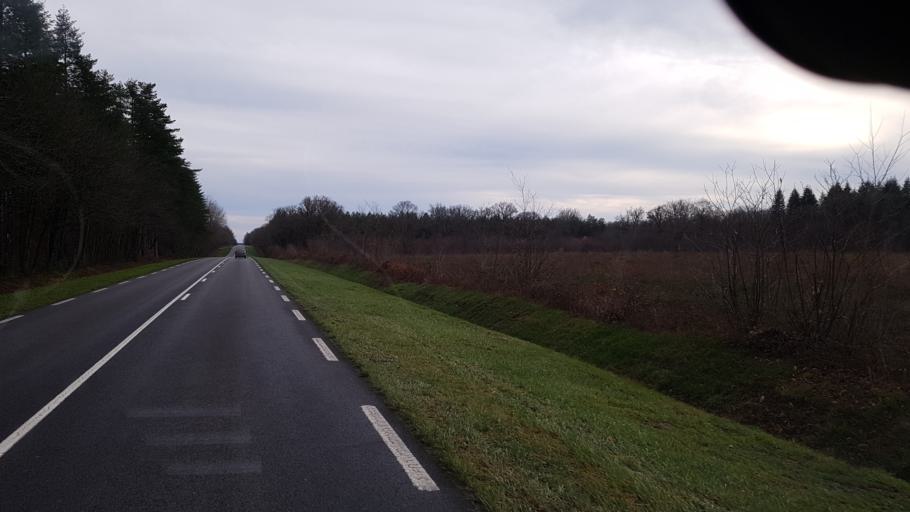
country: FR
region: Centre
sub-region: Departement du Loir-et-Cher
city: Lamotte-Beuvron
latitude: 47.6271
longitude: 2.0078
